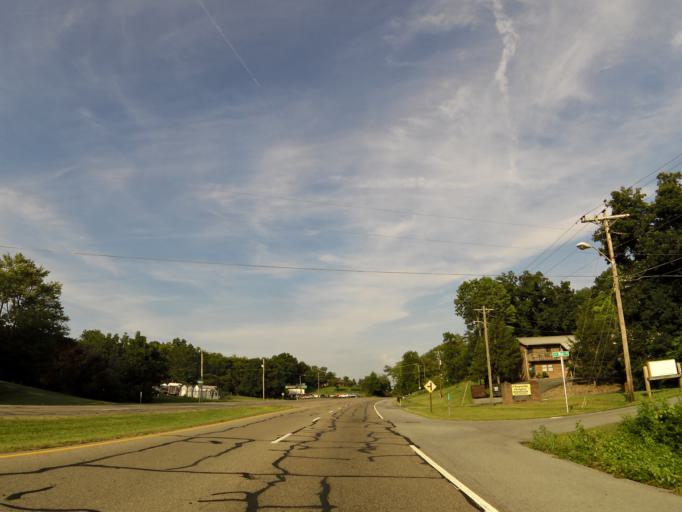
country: US
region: Tennessee
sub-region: Sevier County
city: Sevierville
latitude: 35.8741
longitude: -83.5877
